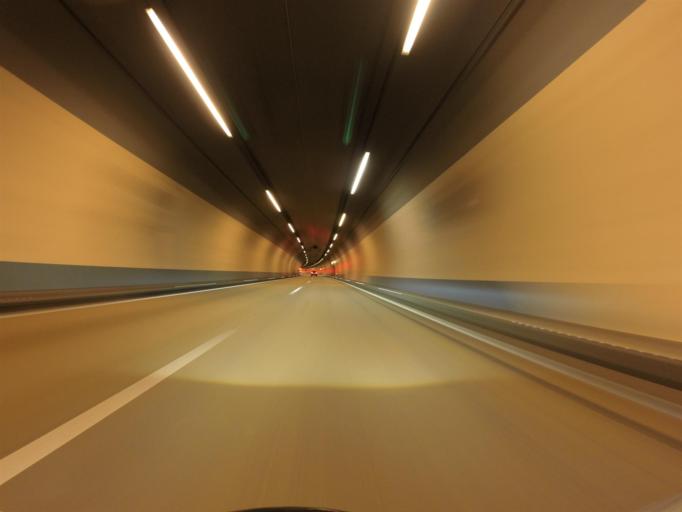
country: LU
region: Grevenmacher
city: Schengen
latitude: 49.4808
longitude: 6.3445
